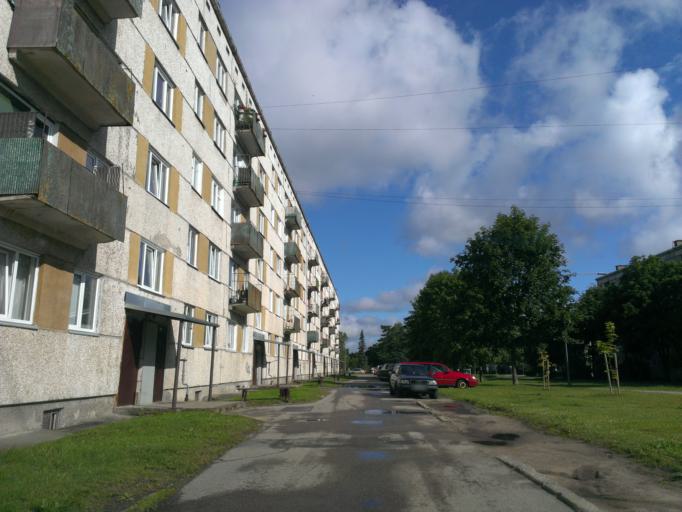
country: LV
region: Incukalns
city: Vangazi
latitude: 57.0892
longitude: 24.5447
